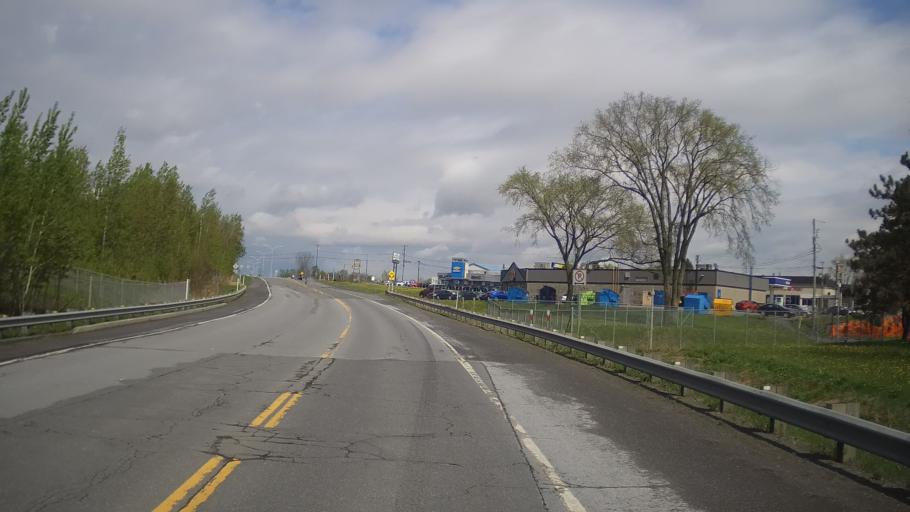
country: CA
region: Quebec
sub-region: Monteregie
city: Cowansville
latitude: 45.2091
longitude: -72.7687
